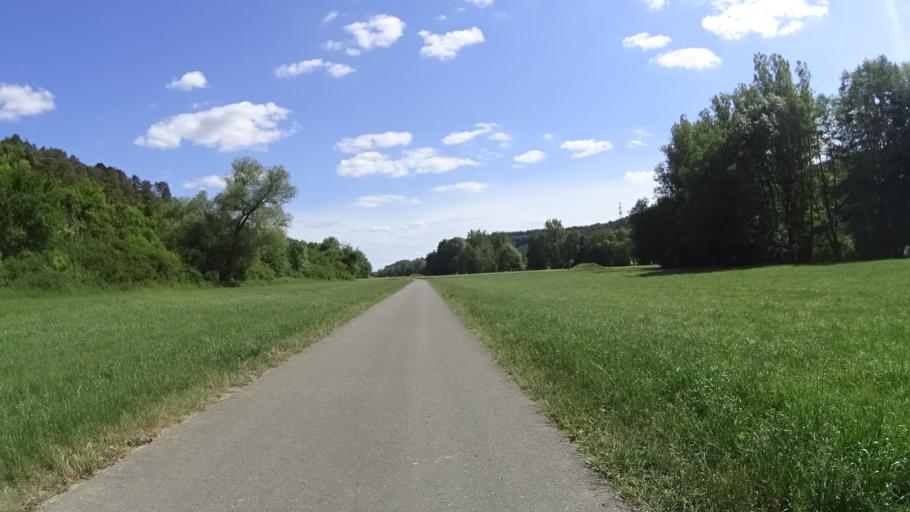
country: DE
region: Baden-Wuerttemberg
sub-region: Karlsruhe Region
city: Hardheim
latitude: 49.5986
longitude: 9.4786
